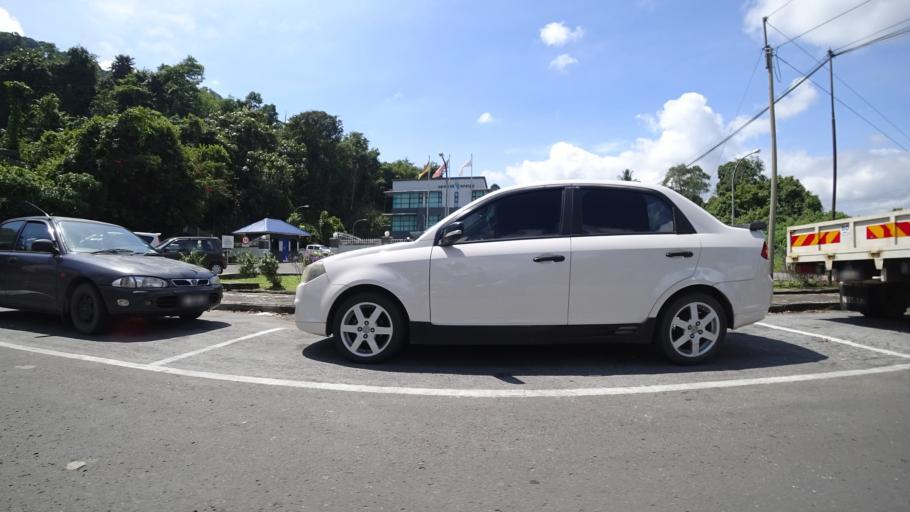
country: MY
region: Sarawak
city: Limbang
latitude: 4.7509
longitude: 115.0093
